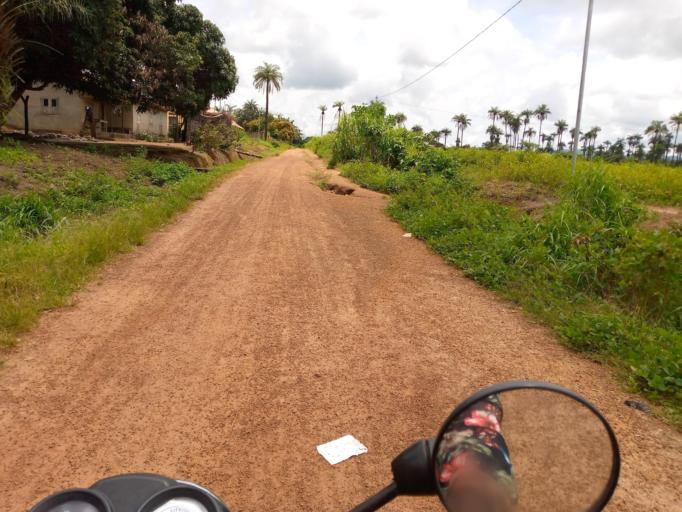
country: SL
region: Northern Province
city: Binkolo
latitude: 9.1109
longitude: -12.1986
